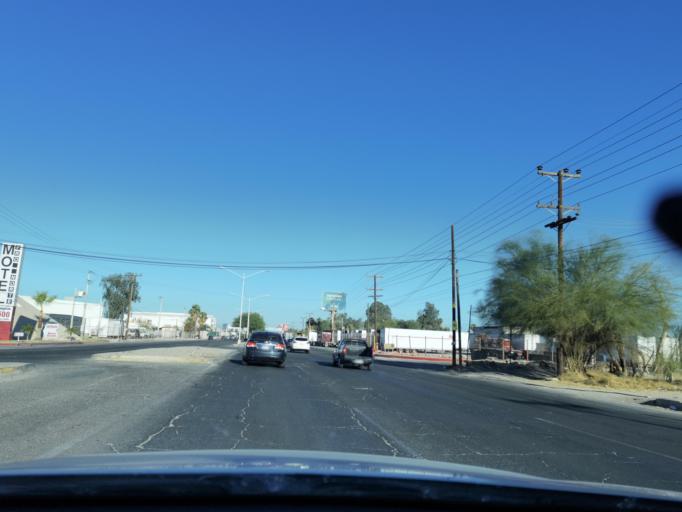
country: MX
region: Baja California
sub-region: Mexicali
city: Islas Agrarias Grupo A
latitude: 32.6530
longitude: -115.3683
